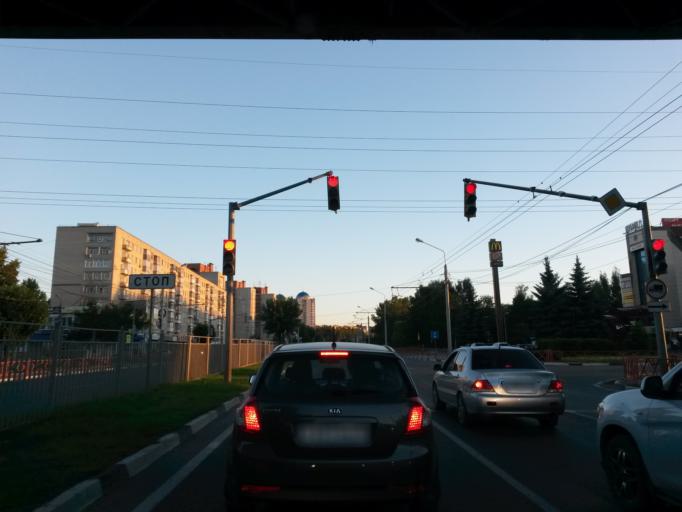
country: RU
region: Jaroslavl
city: Yaroslavl
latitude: 57.5858
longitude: 39.8561
